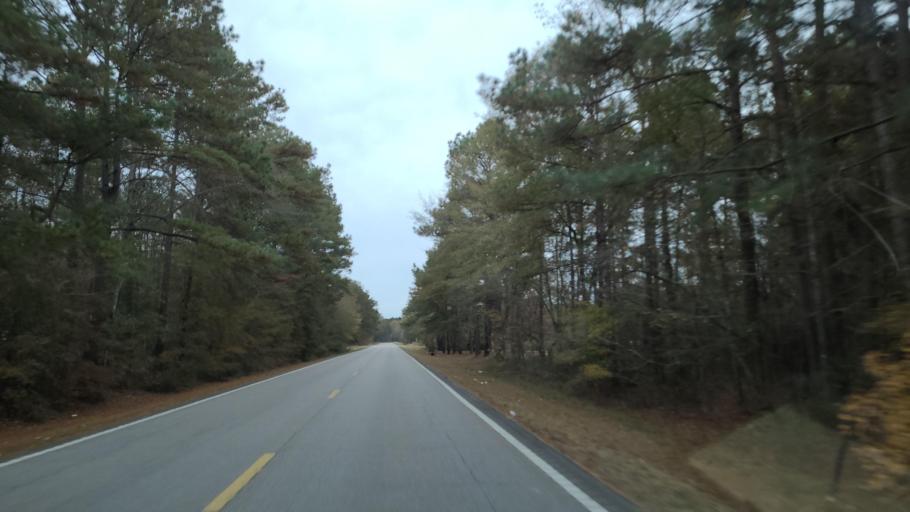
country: US
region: Mississippi
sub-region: Clarke County
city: Stonewall
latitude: 32.0314
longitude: -88.8680
